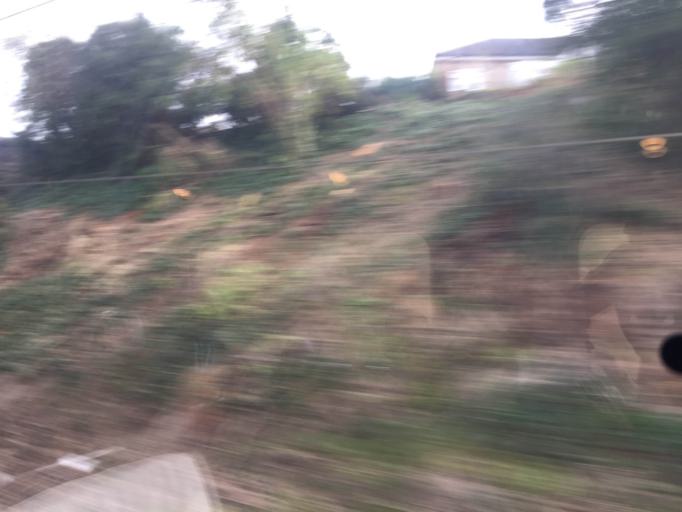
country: GB
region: England
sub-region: Lancashire
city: Lancaster
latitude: 54.0287
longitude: -2.7987
